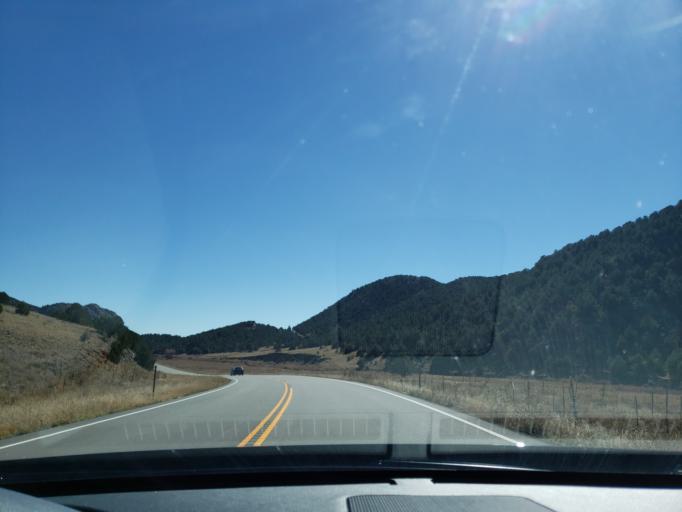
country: US
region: Colorado
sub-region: Fremont County
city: Canon City
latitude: 38.6233
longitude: -105.4561
